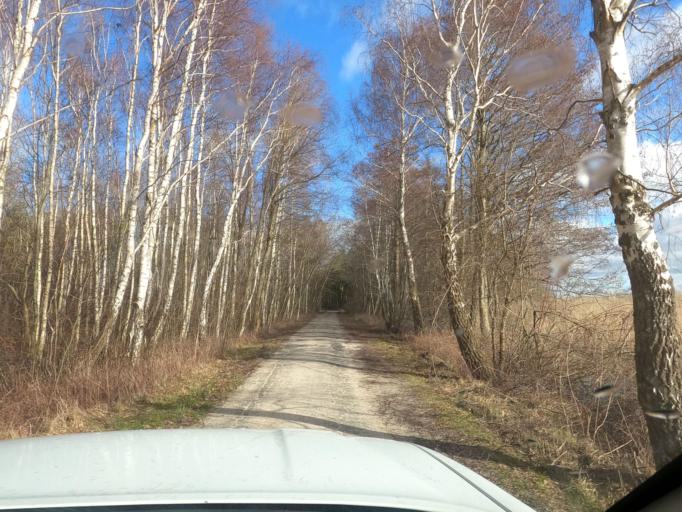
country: PL
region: West Pomeranian Voivodeship
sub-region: Powiat koszalinski
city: Sianow
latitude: 54.3461
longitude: 16.2588
